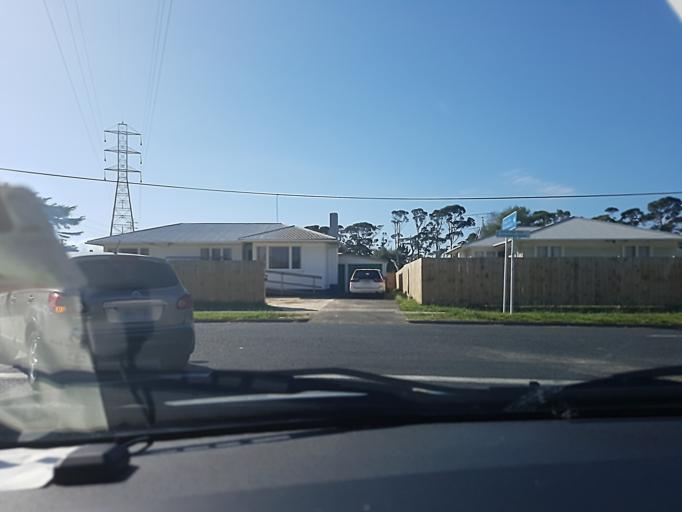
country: NZ
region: Auckland
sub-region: Auckland
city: Tamaki
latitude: -36.9178
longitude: 174.8689
